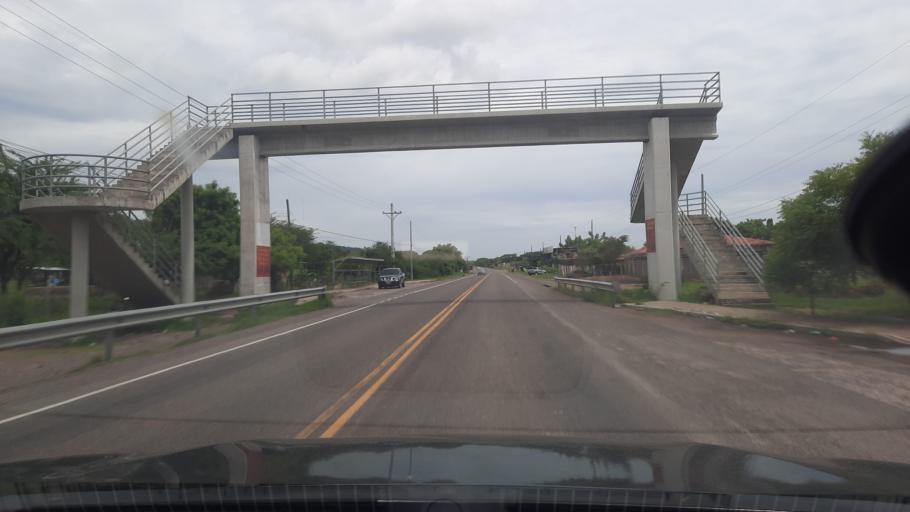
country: HN
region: Valle
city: Jicaro Galan
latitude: 13.5005
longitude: -87.4423
